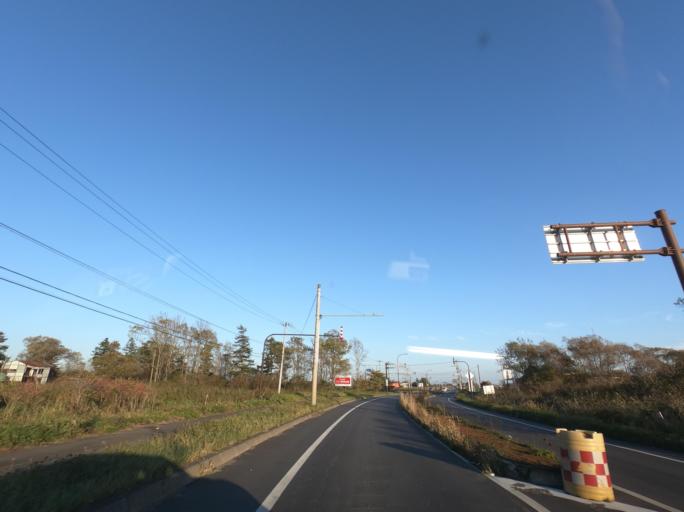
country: JP
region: Hokkaido
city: Kushiro
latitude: 43.0547
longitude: 144.2932
